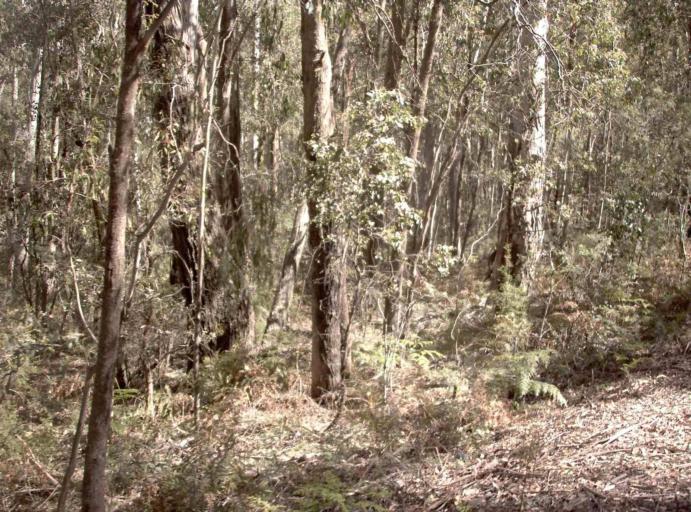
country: AU
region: New South Wales
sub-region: Bombala
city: Bombala
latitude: -37.1212
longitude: 148.7513
